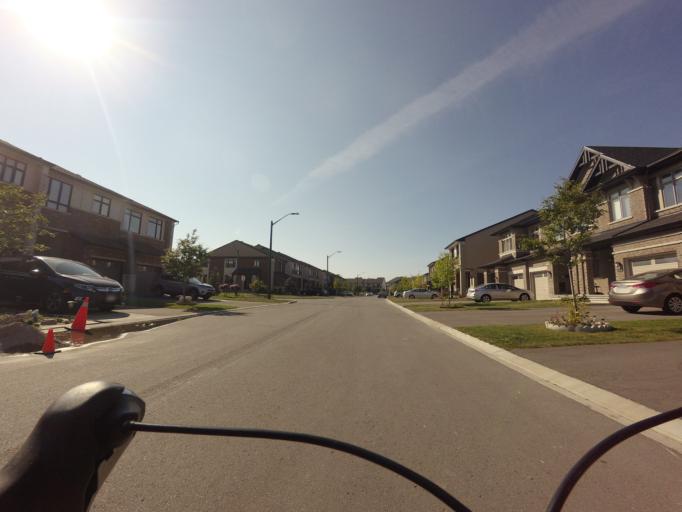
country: CA
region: Ontario
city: Bells Corners
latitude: 45.2679
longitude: -75.6980
